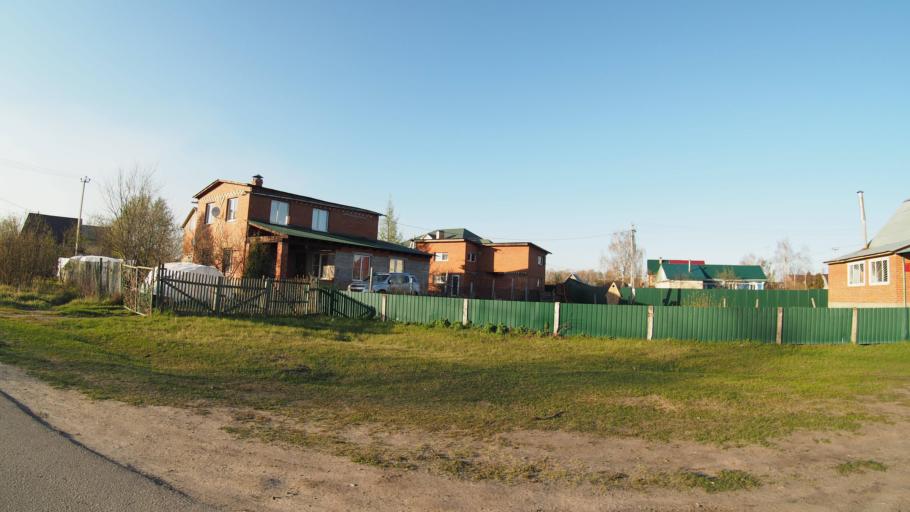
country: RU
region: Moskovskaya
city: Malyshevo
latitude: 55.4934
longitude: 38.3501
